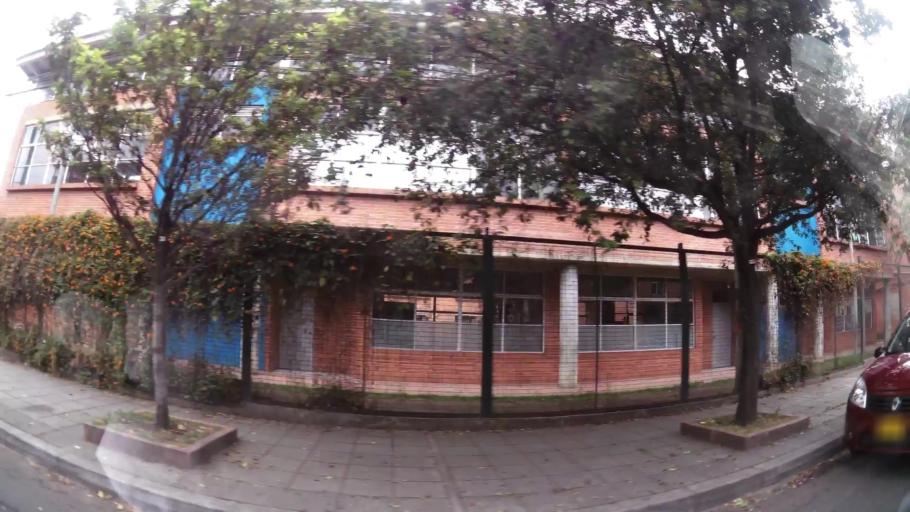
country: CO
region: Bogota D.C.
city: Bogota
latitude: 4.6765
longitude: -74.0898
